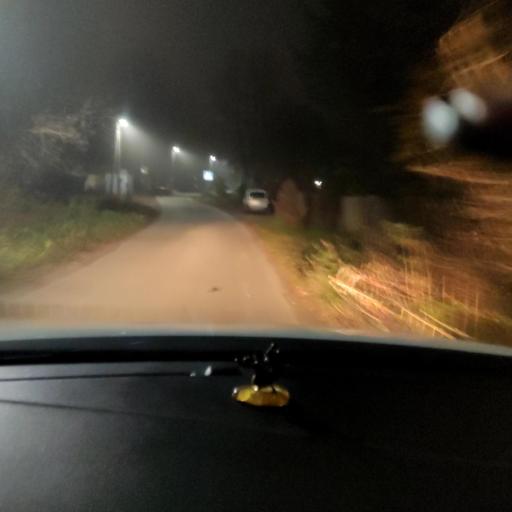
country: RU
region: Tatarstan
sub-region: Gorod Kazan'
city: Kazan
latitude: 55.7504
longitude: 49.1567
